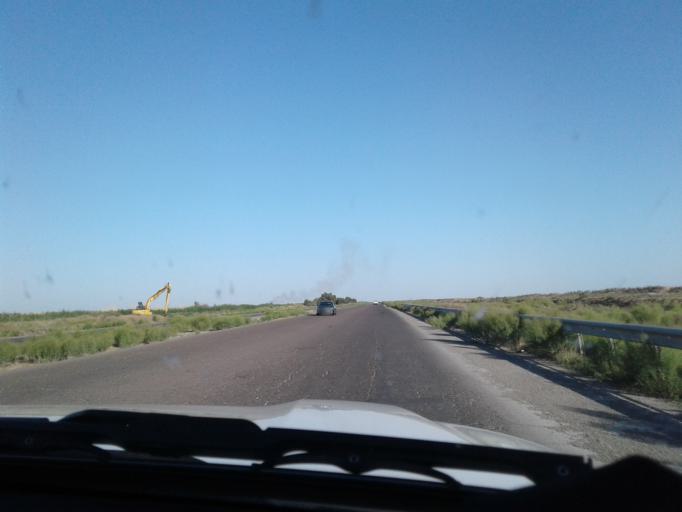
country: TM
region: Ahal
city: Tejen
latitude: 37.2717
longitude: 60.8173
